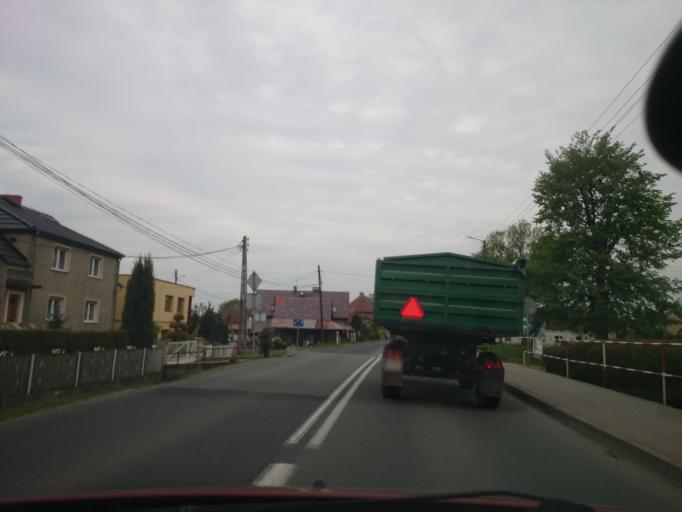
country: PL
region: Opole Voivodeship
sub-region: Powiat opolski
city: Dobrzen Wielki
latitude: 50.7562
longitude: 17.8483
